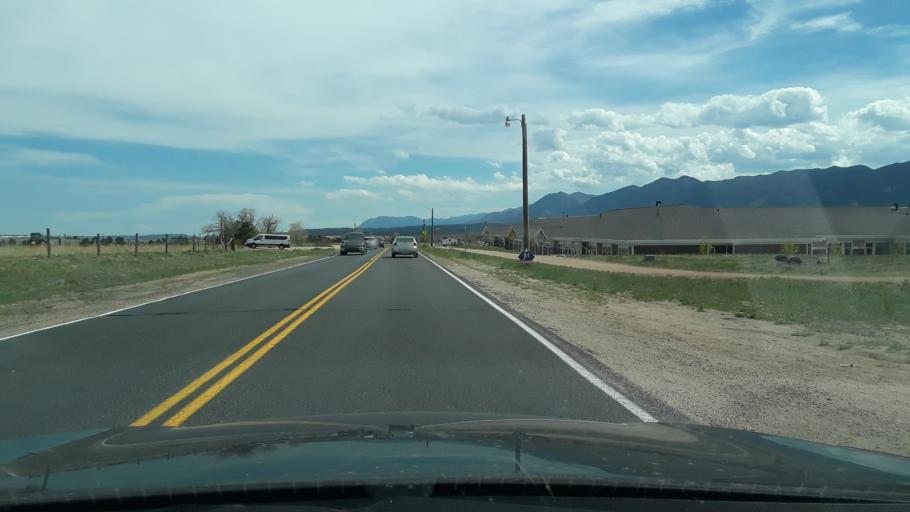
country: US
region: Colorado
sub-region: El Paso County
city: Monument
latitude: 39.0904
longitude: -104.8683
